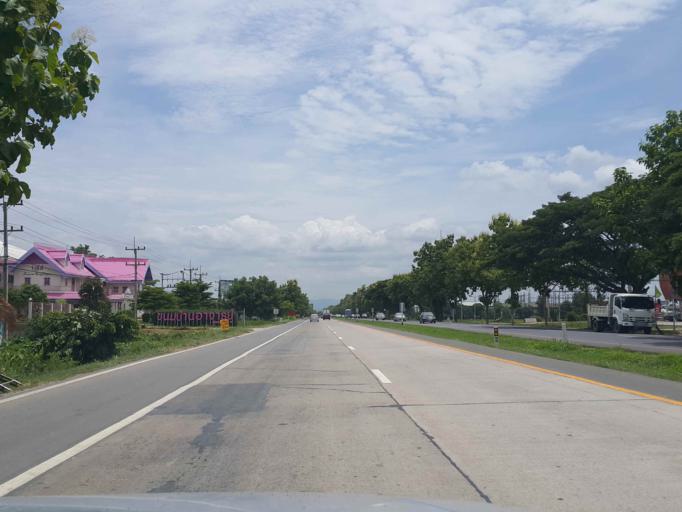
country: TH
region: Chiang Mai
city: Saraphi
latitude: 18.6600
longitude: 99.0524
